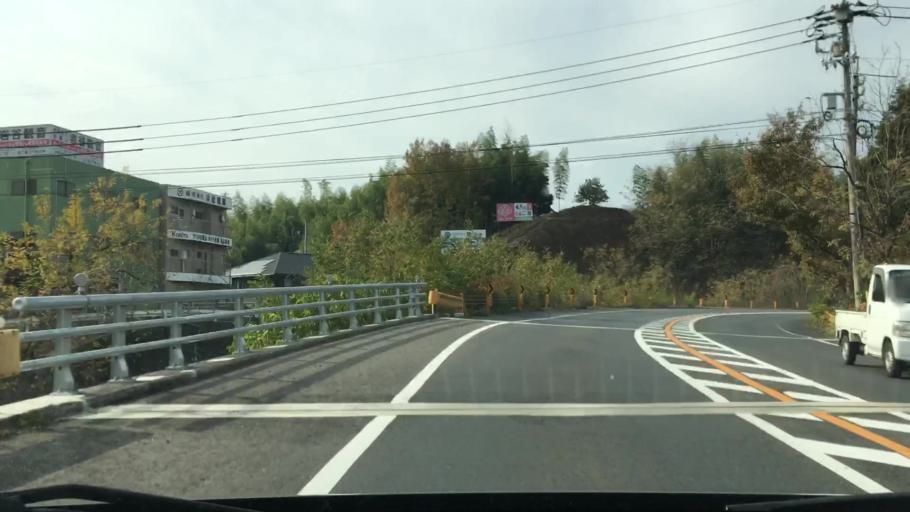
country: JP
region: Yamaguchi
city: Iwakuni
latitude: 34.1539
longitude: 132.1869
